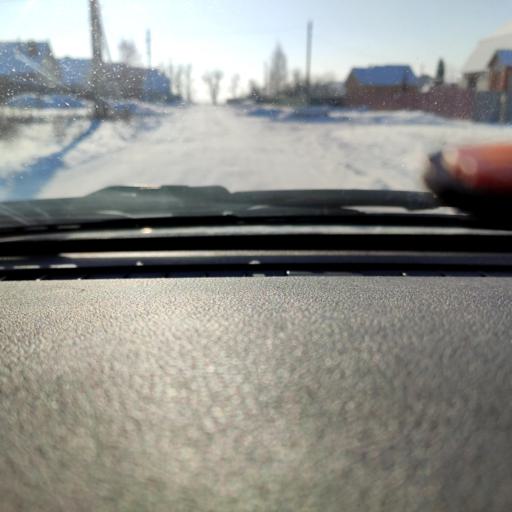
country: RU
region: Voronezj
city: Novaya Usman'
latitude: 51.6068
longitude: 39.3788
